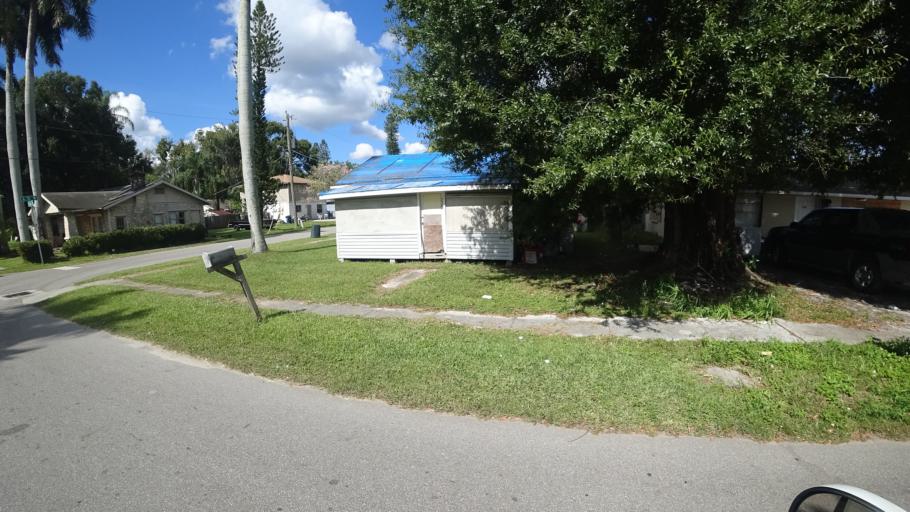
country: US
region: Florida
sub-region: Manatee County
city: West Samoset
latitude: 27.4756
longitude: -82.5679
